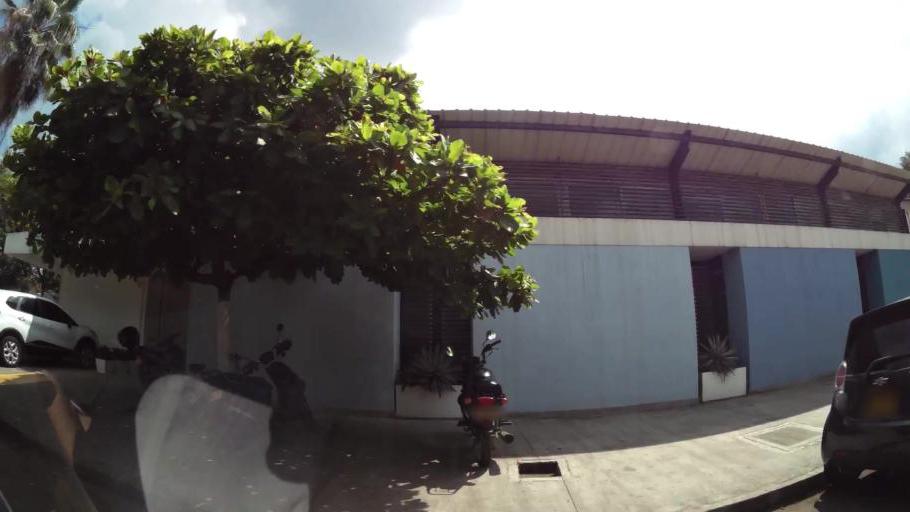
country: CO
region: Valle del Cauca
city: Cali
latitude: 3.4858
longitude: -76.5020
